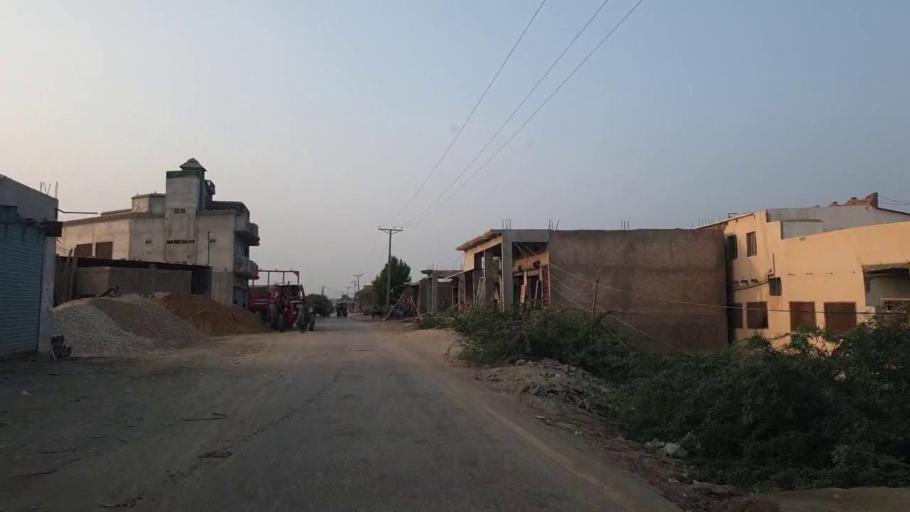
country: PK
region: Sindh
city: Tando Ghulam Ali
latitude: 25.1440
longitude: 68.9576
